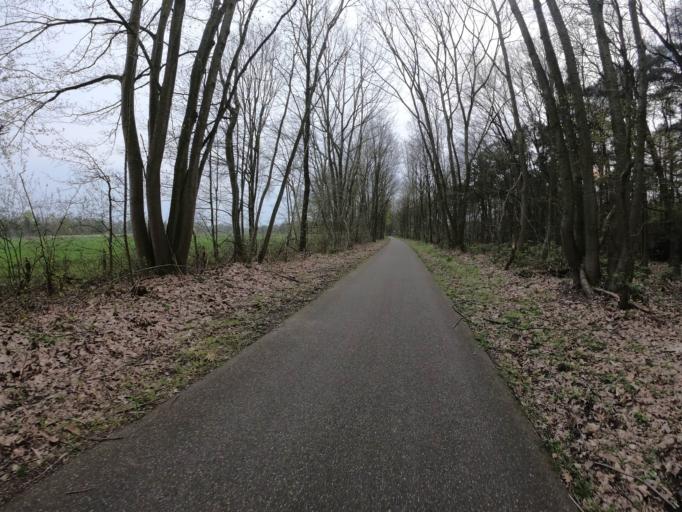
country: BE
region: Flanders
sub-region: Provincie Limburg
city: Maaseik
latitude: 51.0773
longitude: 5.7371
